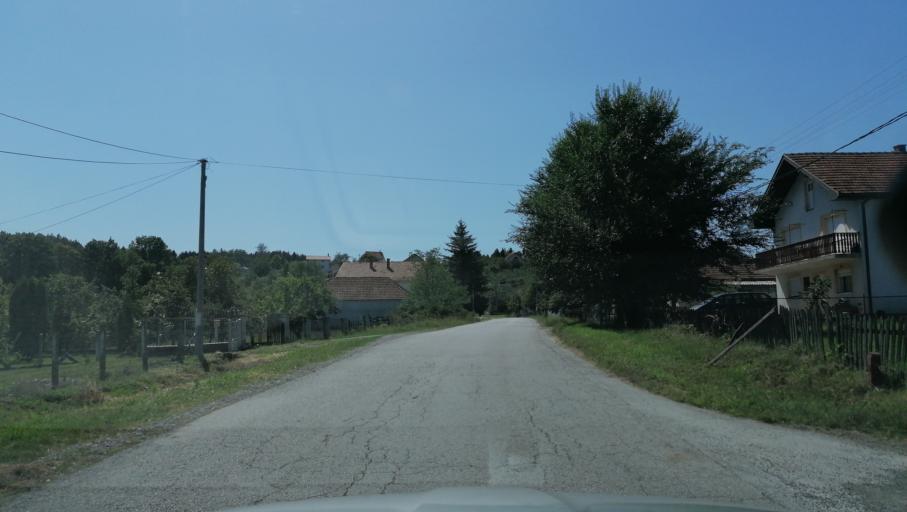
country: RS
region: Central Serbia
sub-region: Kolubarski Okrug
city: Valjevo
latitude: 44.2553
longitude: 19.8763
